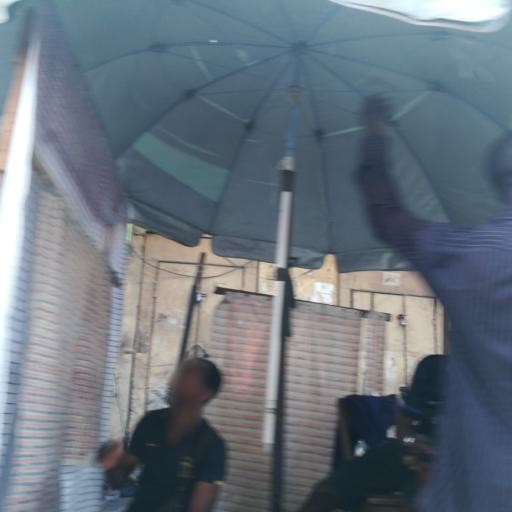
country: NG
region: Lagos
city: Lagos
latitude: 6.4629
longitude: 3.3894
